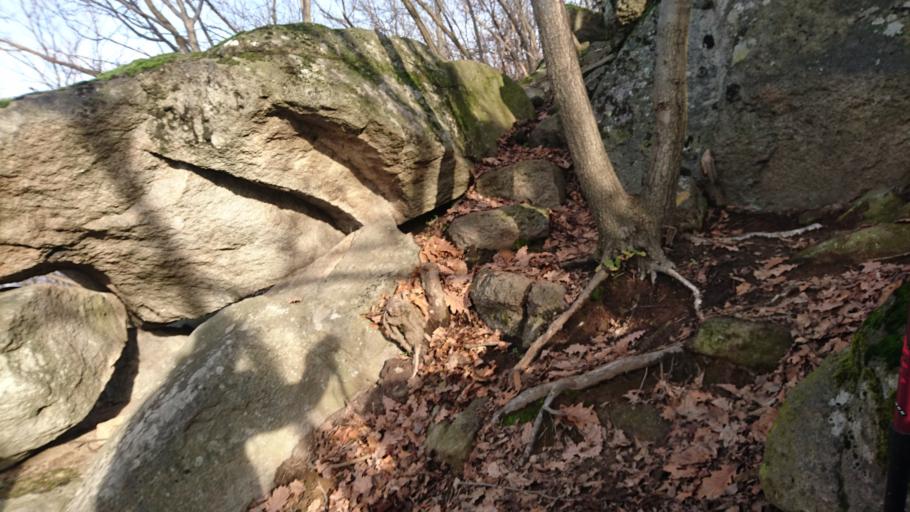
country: IT
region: Veneto
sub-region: Provincia di Padova
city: Treponti
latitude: 45.3350
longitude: 11.6846
